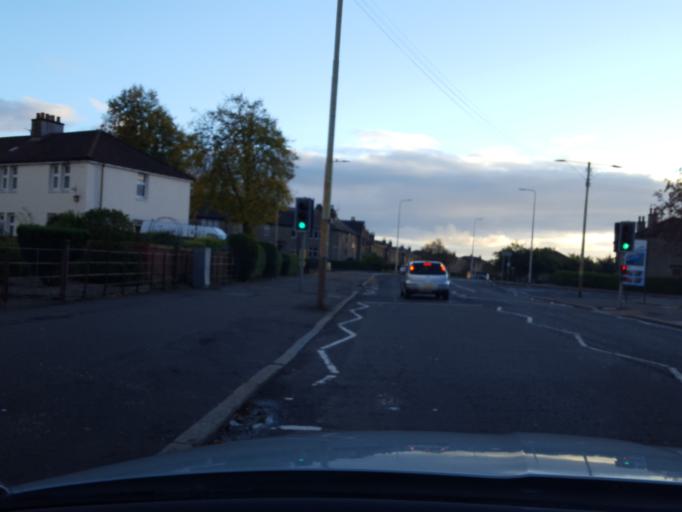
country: GB
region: Scotland
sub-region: Dundee City
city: Dundee
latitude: 56.4727
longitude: -2.9947
